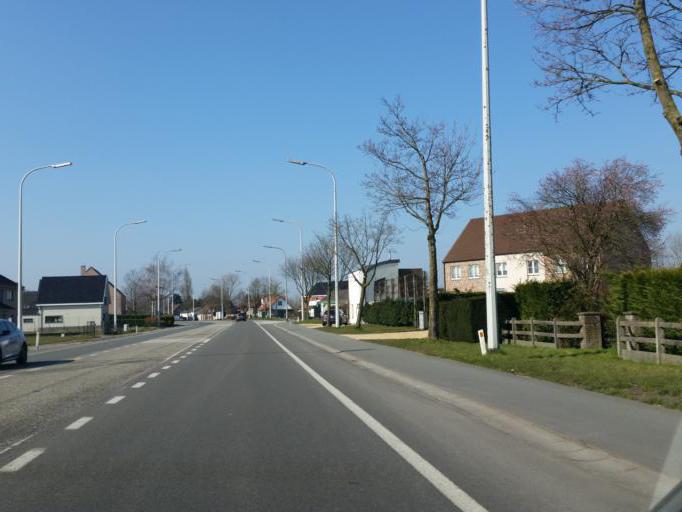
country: BE
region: Flanders
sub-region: Provincie Oost-Vlaanderen
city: Lokeren
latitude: 51.1129
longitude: 3.9593
